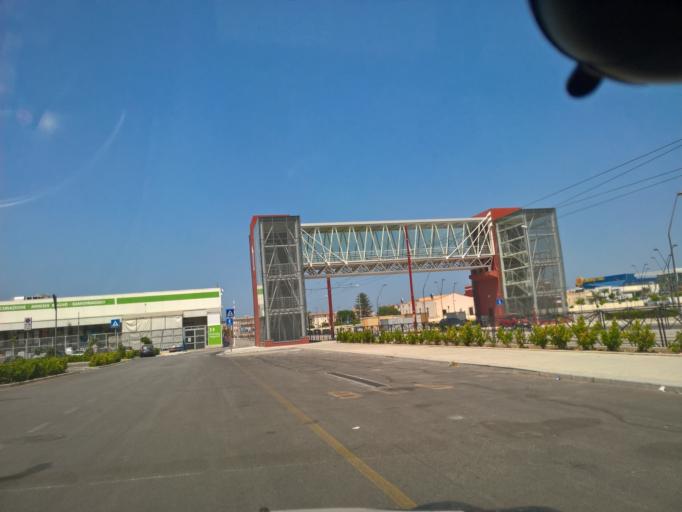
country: IT
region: Sicily
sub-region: Palermo
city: Ciaculli
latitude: 38.0893
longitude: 13.4089
